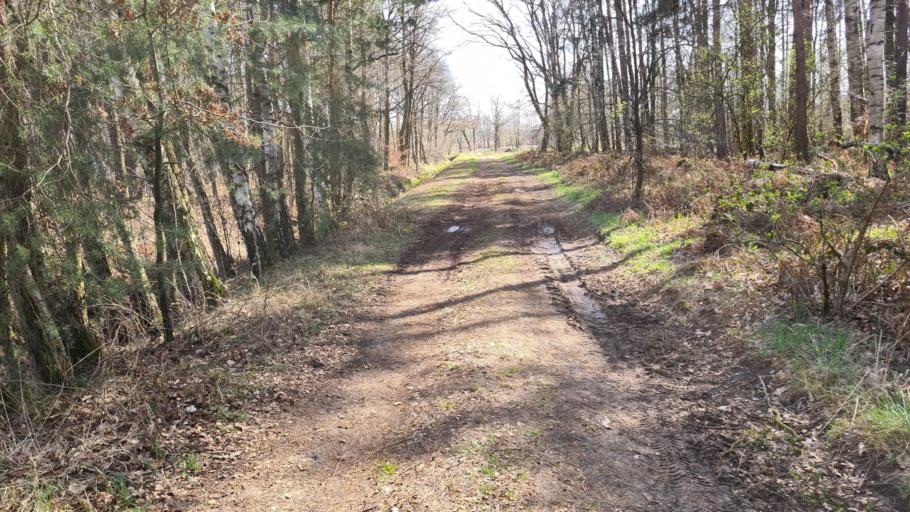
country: DE
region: Brandenburg
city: Finsterwalde
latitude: 51.6006
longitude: 13.6430
